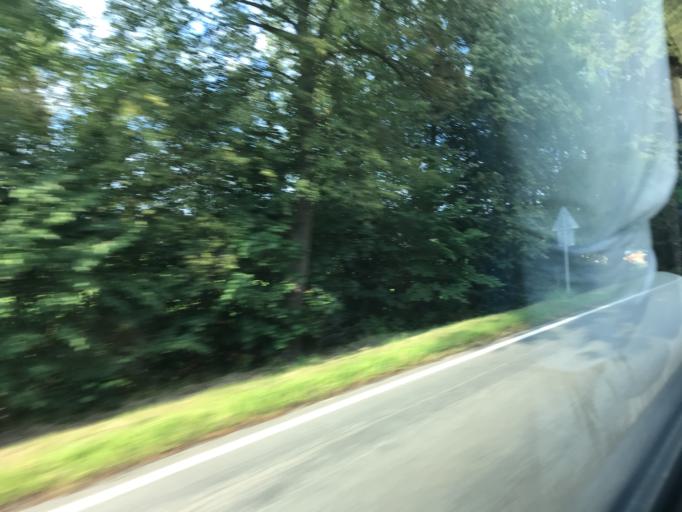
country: CZ
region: Jihocesky
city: Rudolfov
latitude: 49.0053
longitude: 14.5585
